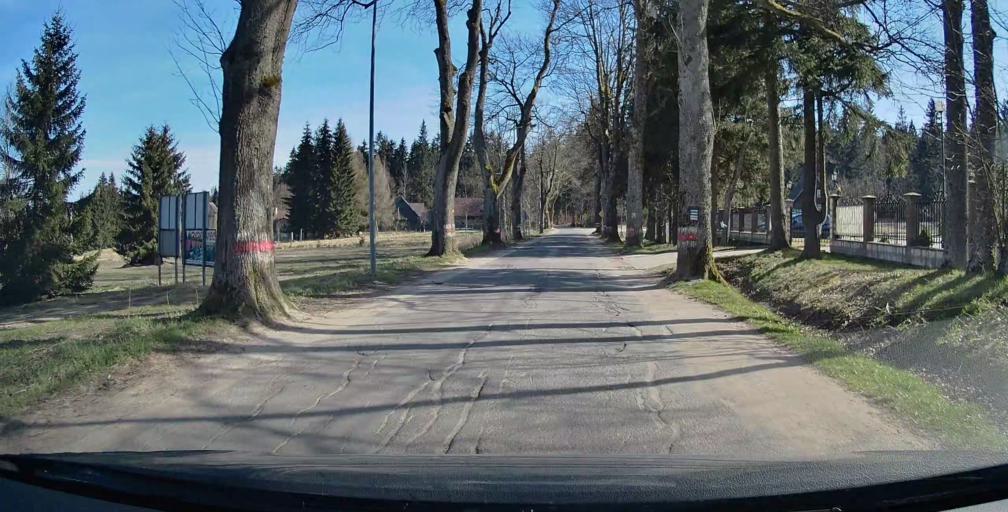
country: CZ
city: Machov
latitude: 50.4746
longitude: 16.3377
